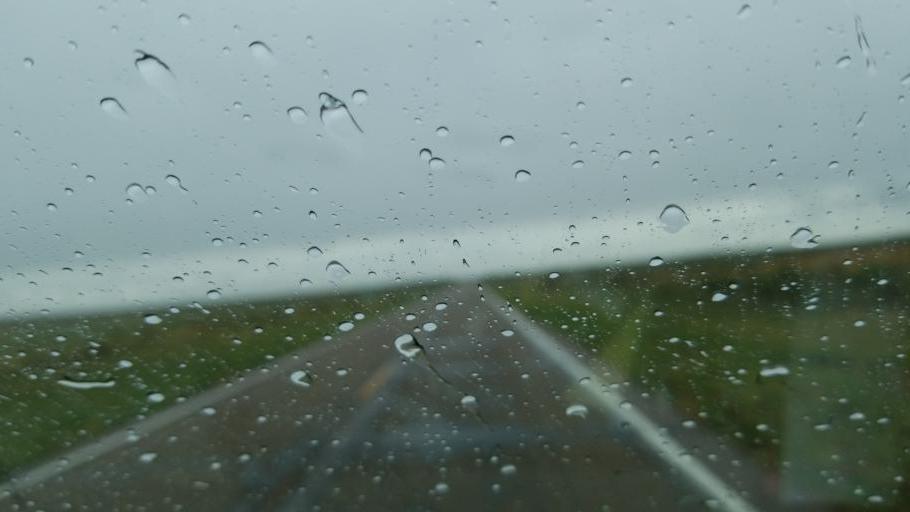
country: US
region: Colorado
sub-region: Lincoln County
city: Hugo
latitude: 38.8497
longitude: -103.1932
